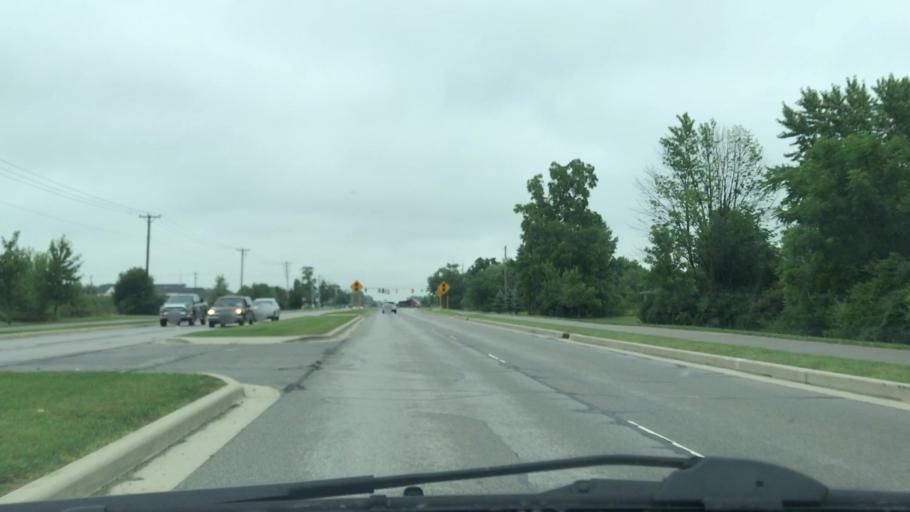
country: US
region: Indiana
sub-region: Hamilton County
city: Westfield
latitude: 40.0405
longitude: -86.0707
